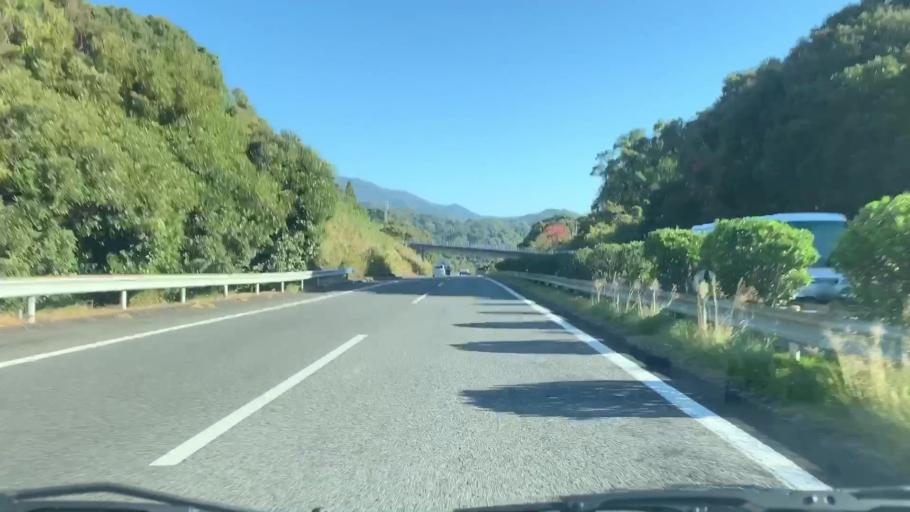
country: JP
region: Saga Prefecture
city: Saga-shi
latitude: 33.2908
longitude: 130.1653
